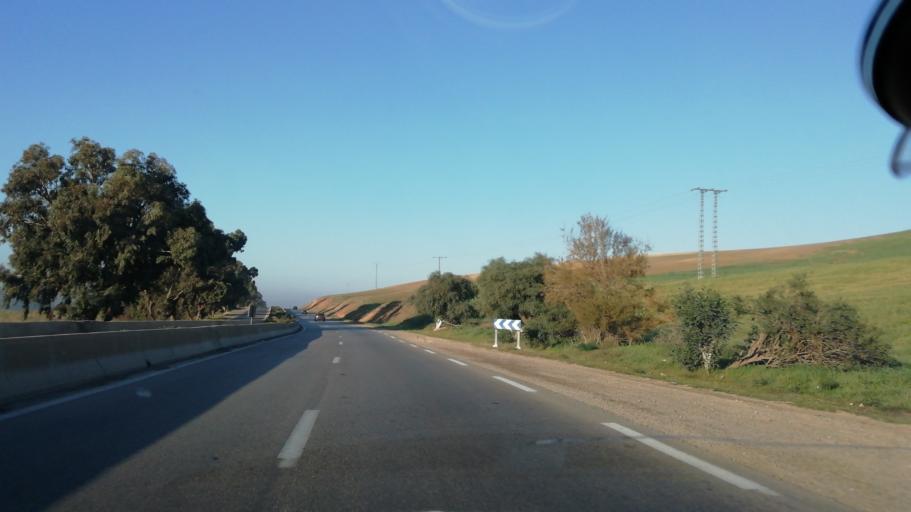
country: DZ
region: Ain Temouchent
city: Beni Saf
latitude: 35.2342
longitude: -1.3436
